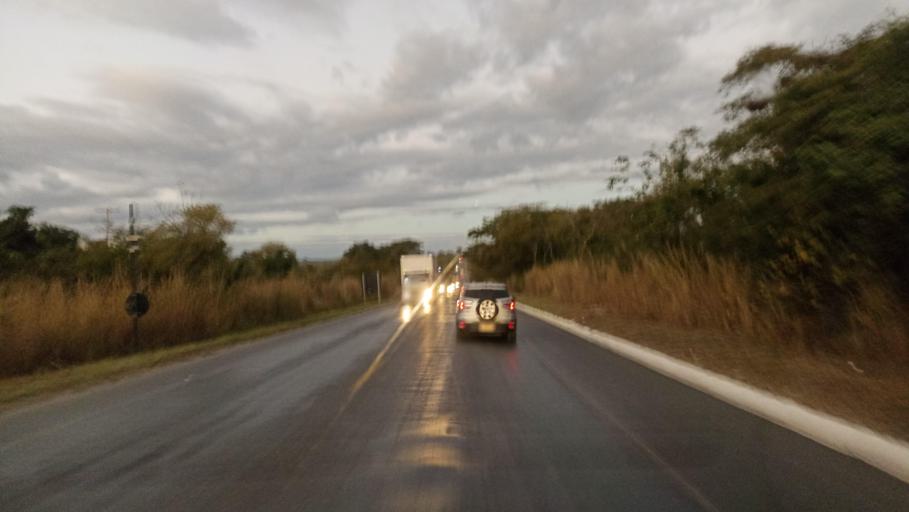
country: BR
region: Minas Gerais
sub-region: Montes Claros
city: Montes Claros
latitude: -16.6585
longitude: -43.7346
